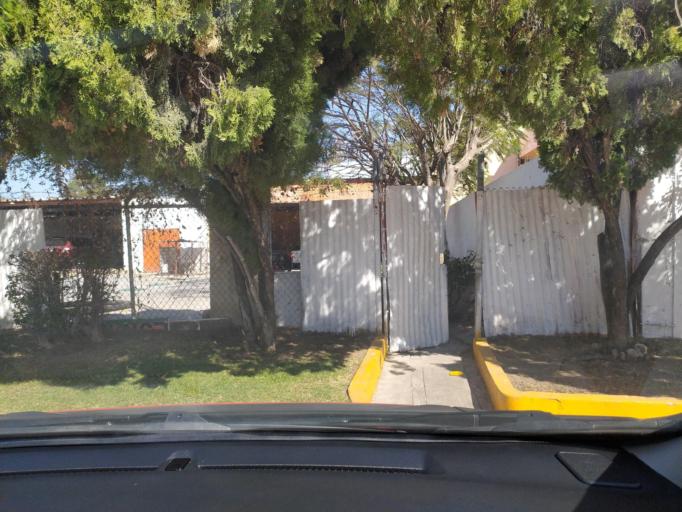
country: LA
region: Oudomxai
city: Muang La
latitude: 21.0293
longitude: 101.8629
